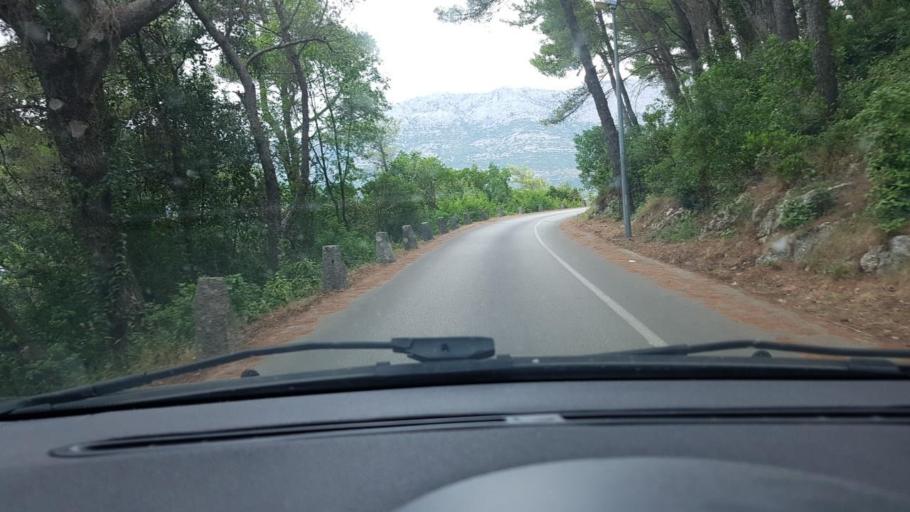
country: HR
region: Dubrovacko-Neretvanska
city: Korcula
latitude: 42.9604
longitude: 17.1279
